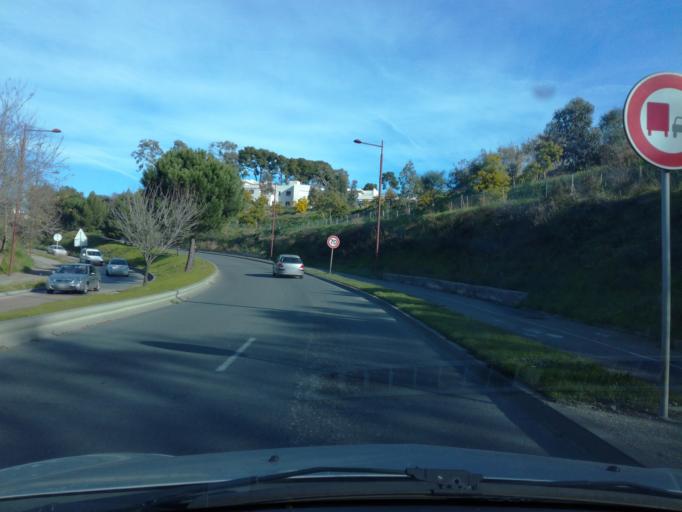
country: FR
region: Provence-Alpes-Cote d'Azur
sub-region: Departement des Alpes-Maritimes
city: Vallauris
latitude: 43.5862
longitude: 7.0916
